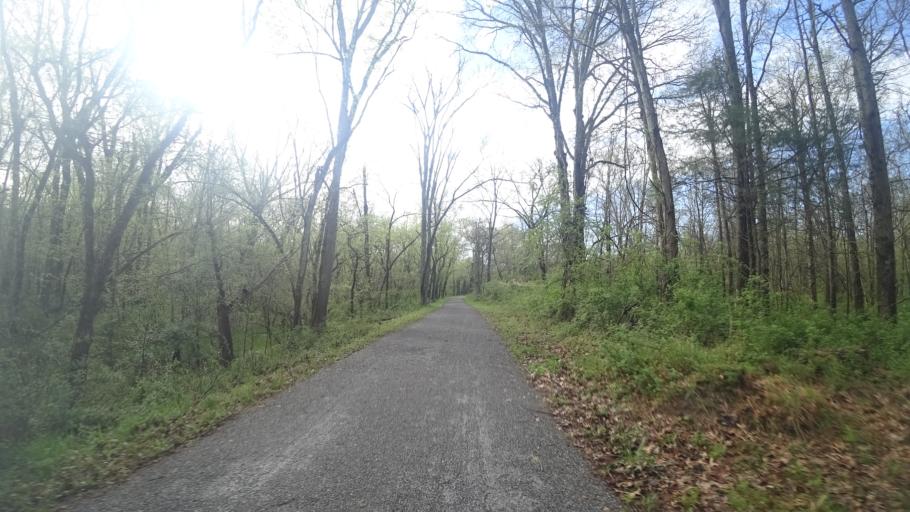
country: US
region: Virginia
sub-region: Loudoun County
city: Belmont
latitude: 39.1085
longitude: -77.4752
